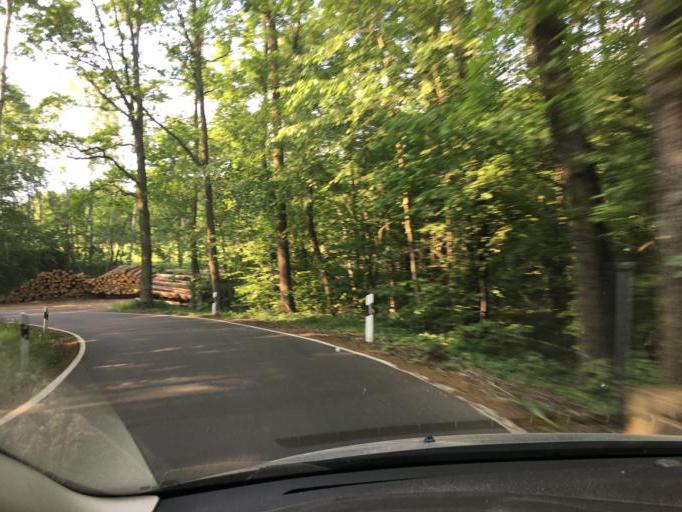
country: DE
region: Saxony
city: Grossbothen
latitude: 51.1957
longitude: 12.7265
